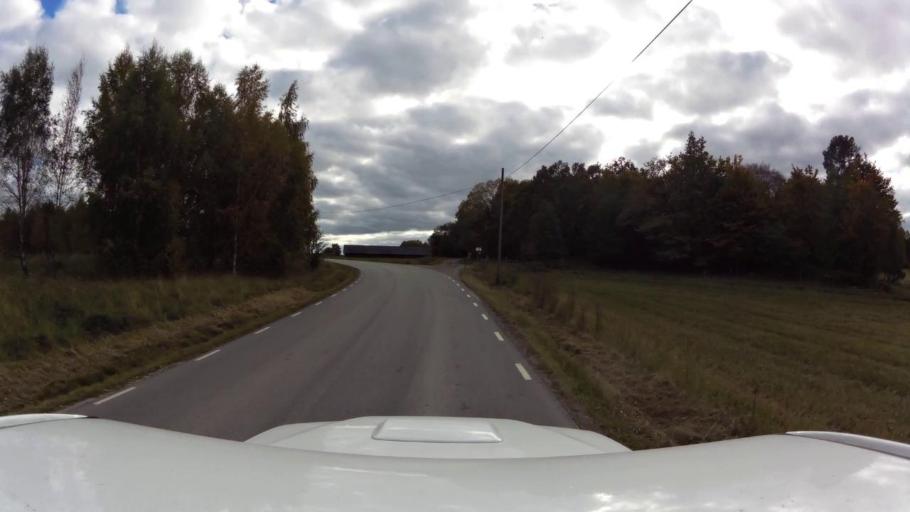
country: SE
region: OEstergoetland
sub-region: Linkopings Kommun
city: Linkoping
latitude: 58.3822
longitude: 15.5924
